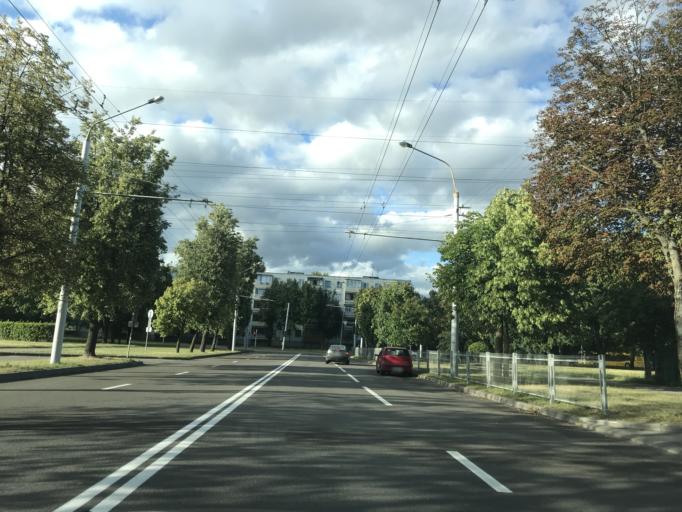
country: BY
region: Minsk
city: Minsk
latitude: 53.9468
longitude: 27.6237
